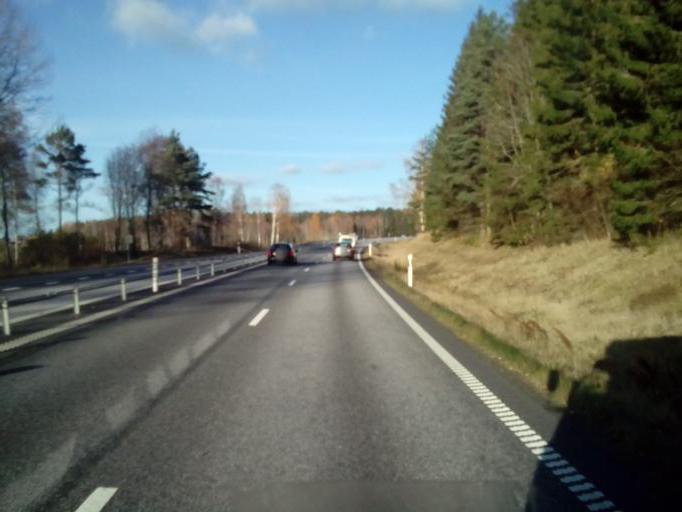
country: SE
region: Kalmar
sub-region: Vimmerby Kommun
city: Vimmerby
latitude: 57.6998
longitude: 16.0166
